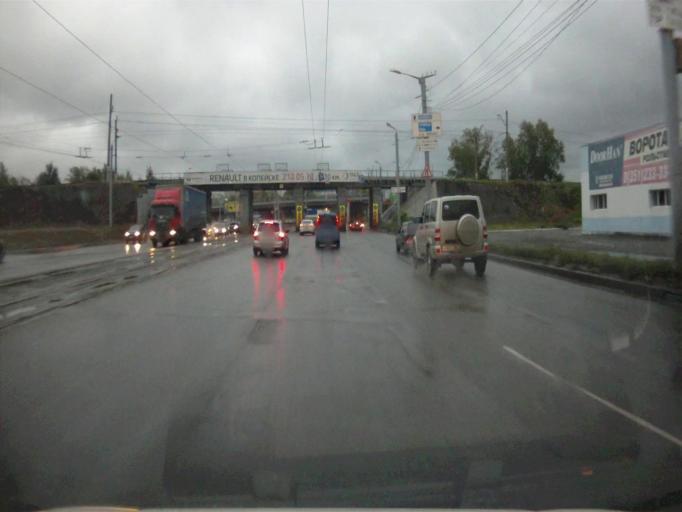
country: RU
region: Chelyabinsk
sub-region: Gorod Chelyabinsk
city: Chelyabinsk
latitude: 55.1529
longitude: 61.4427
